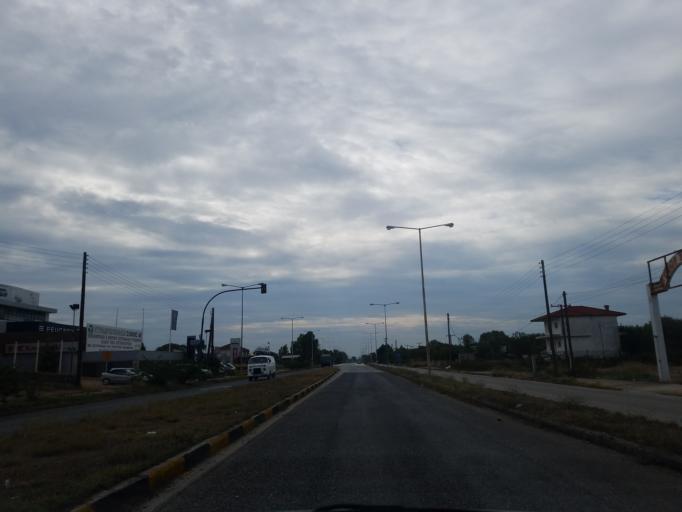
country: GR
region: Thessaly
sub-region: Trikala
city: Pyrgetos
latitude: 39.5848
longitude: 21.7391
